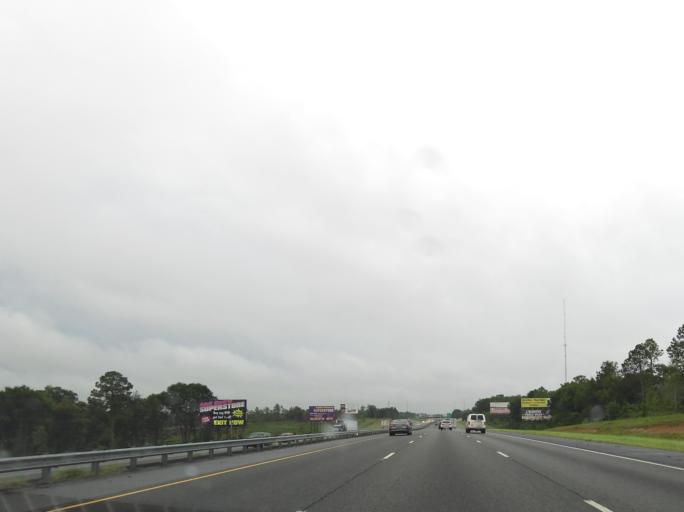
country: US
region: Georgia
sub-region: Crisp County
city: Cordele
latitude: 31.9156
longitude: -83.7413
